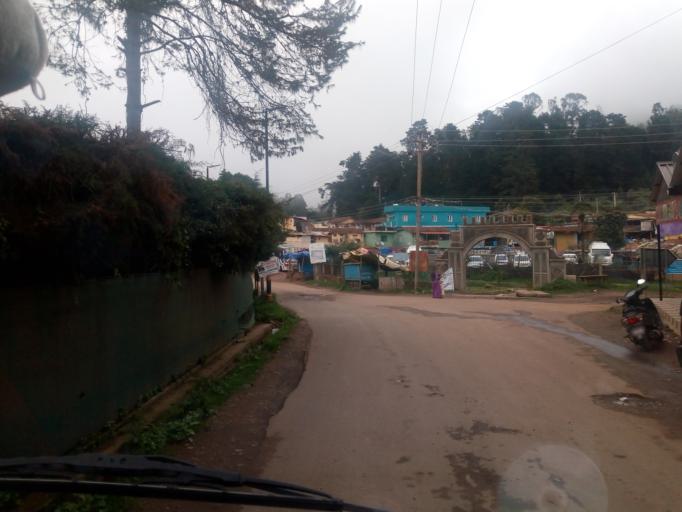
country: IN
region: Tamil Nadu
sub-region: Nilgiri
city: Ooty
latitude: 11.4148
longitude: 76.7125
